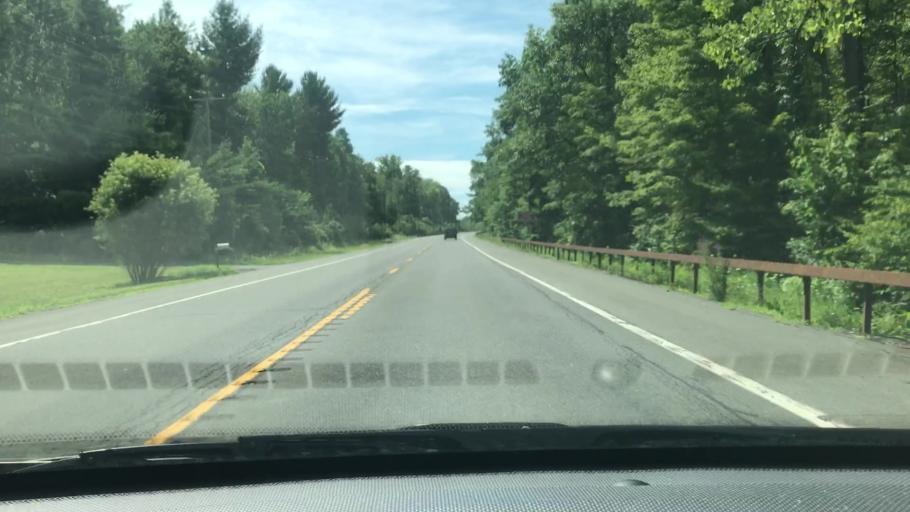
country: US
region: New York
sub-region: Ulster County
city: Shokan
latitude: 41.9927
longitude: -74.2629
